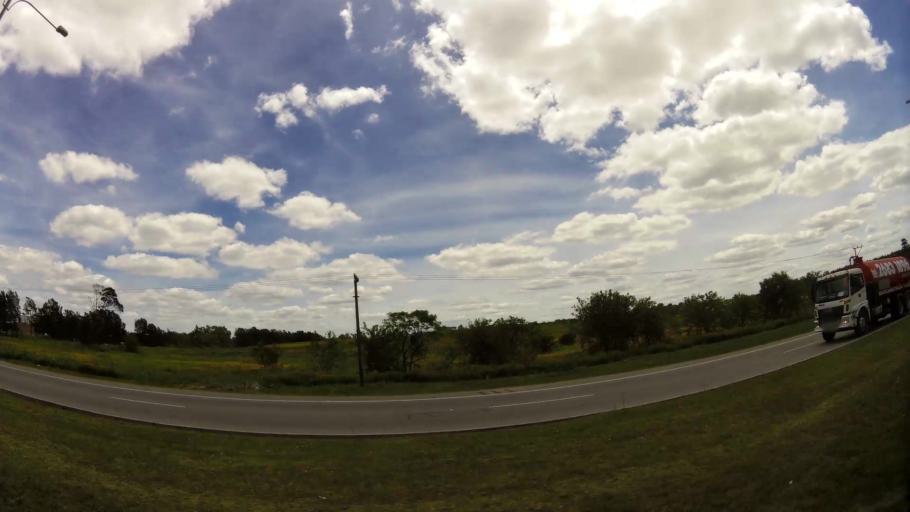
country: UY
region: Canelones
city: Colonia Nicolich
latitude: -34.8257
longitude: -55.9985
